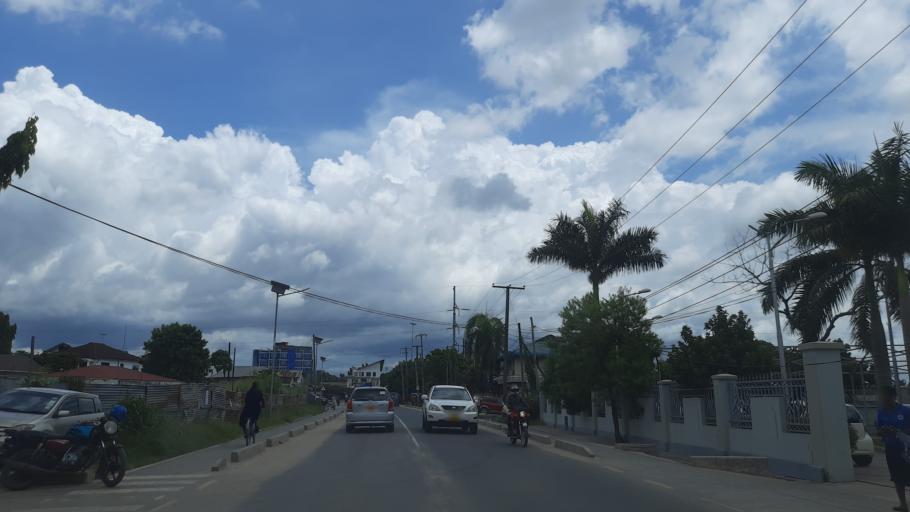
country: TZ
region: Dar es Salaam
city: Magomeni
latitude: -6.7691
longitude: 39.2271
